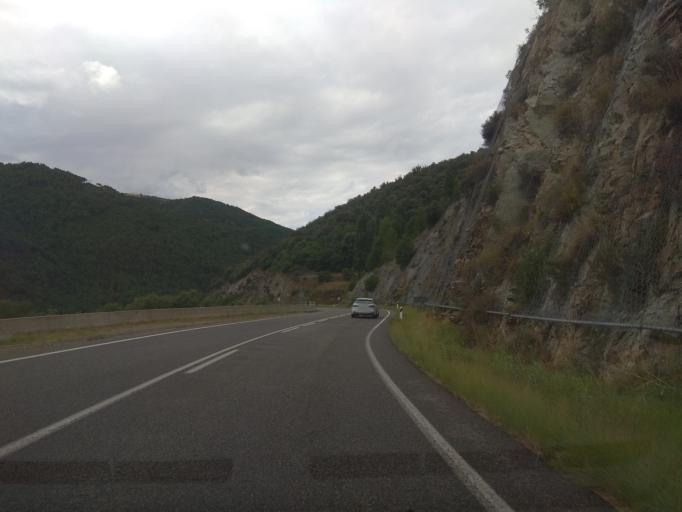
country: ES
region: Catalonia
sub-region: Provincia de Lleida
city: el Pont de Bar
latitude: 42.3617
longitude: 1.5723
